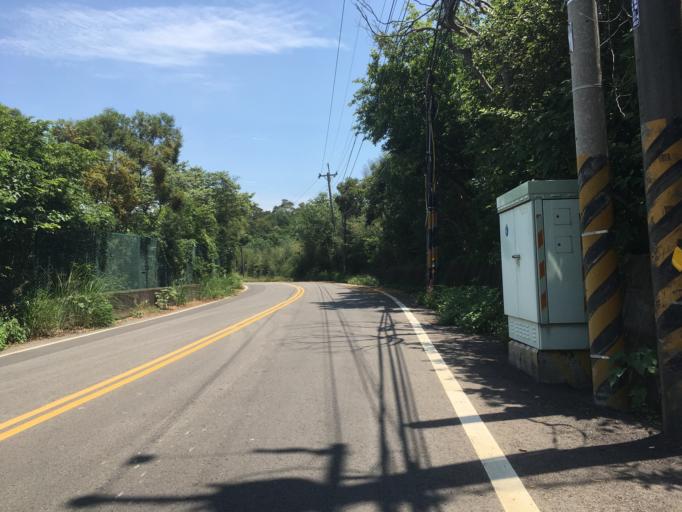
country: TW
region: Taiwan
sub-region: Hsinchu
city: Hsinchu
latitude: 24.7395
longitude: 120.9848
